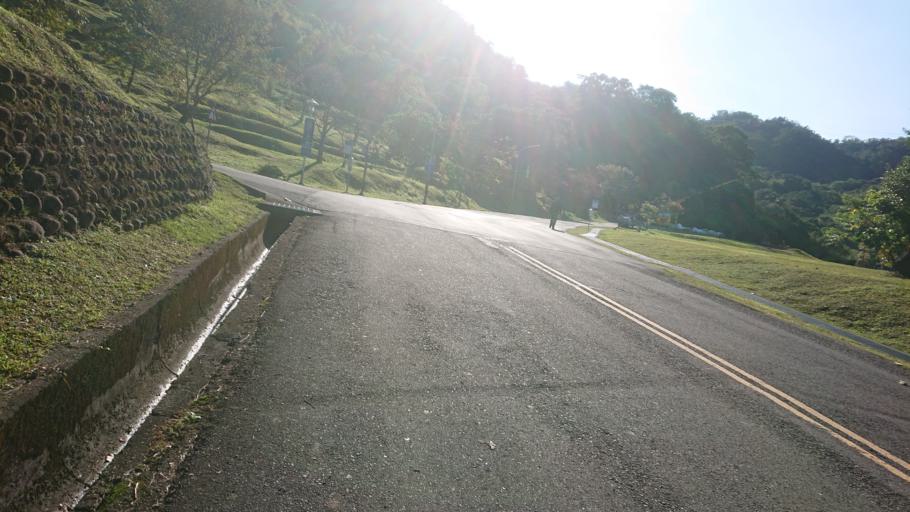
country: TW
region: Taipei
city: Taipei
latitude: 24.9787
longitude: 121.5735
